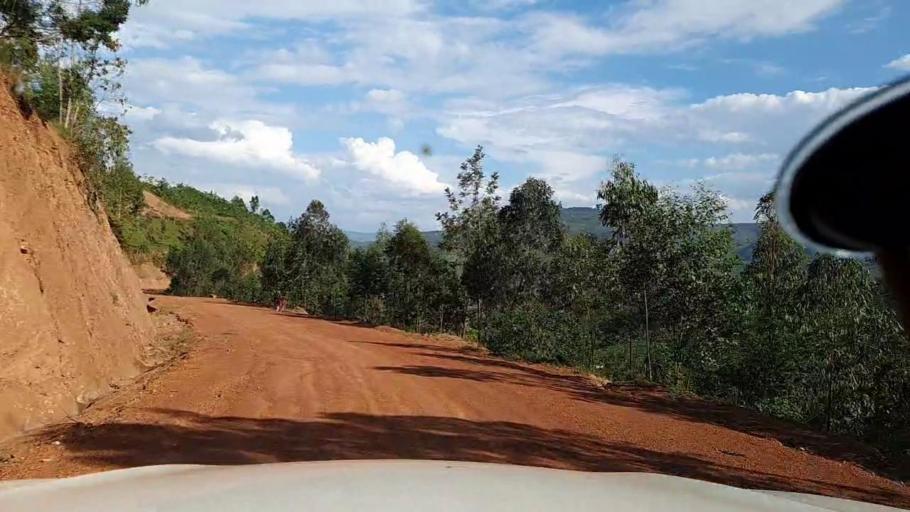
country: RW
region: Kigali
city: Kigali
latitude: -1.8466
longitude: 29.8611
